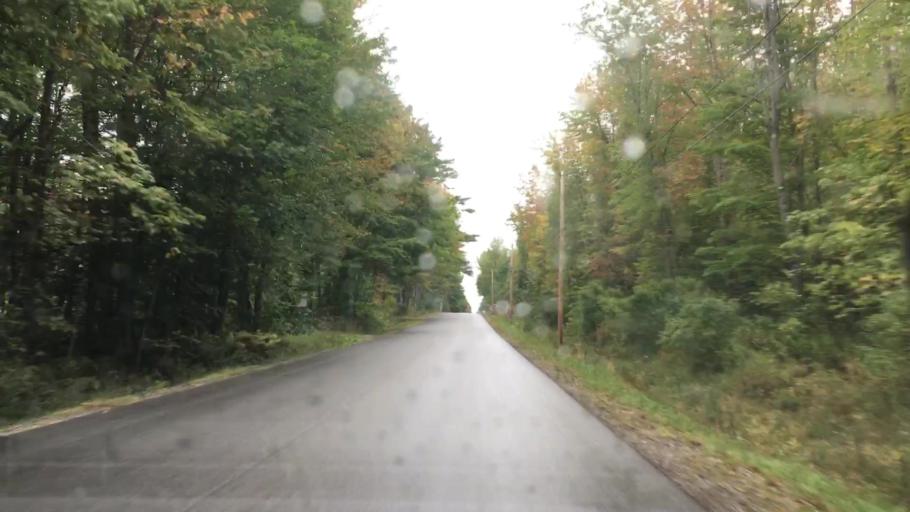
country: US
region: Maine
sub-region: Cumberland County
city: Harrison
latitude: 44.0926
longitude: -70.6555
